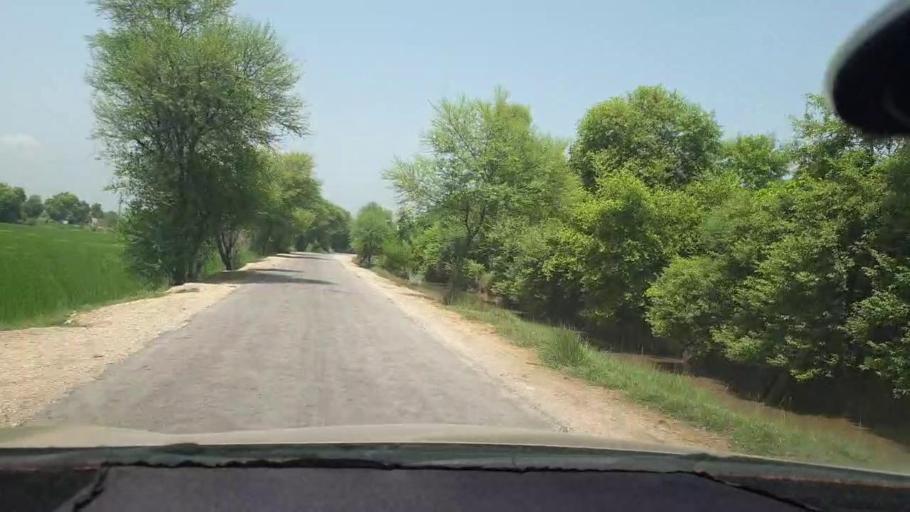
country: PK
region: Sindh
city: Kambar
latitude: 27.6470
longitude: 67.9699
